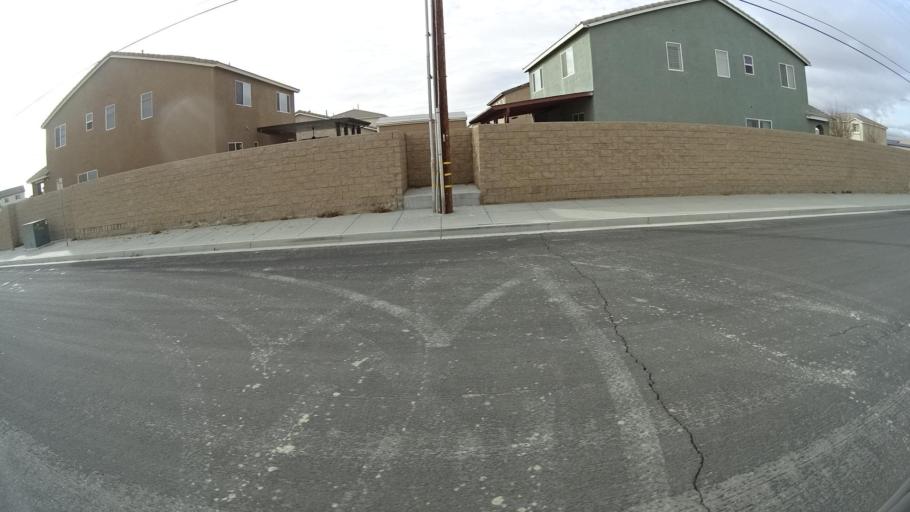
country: US
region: California
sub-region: Kern County
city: Rosamond
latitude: 34.8520
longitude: -118.1849
